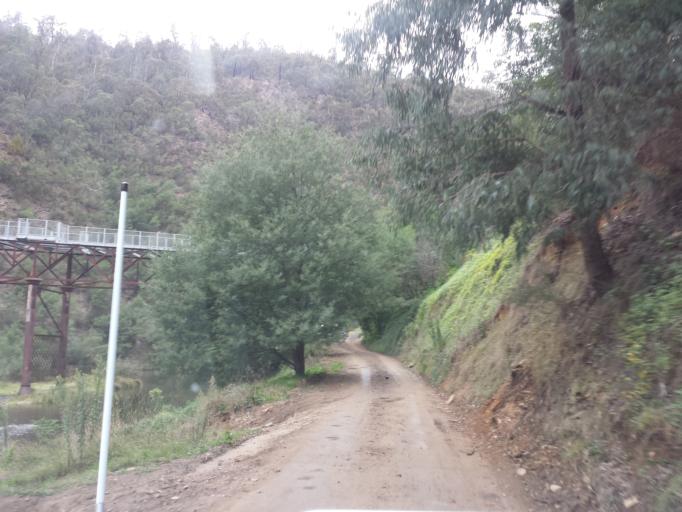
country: AU
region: Victoria
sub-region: Latrobe
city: Traralgon
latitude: -37.9987
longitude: 146.4724
